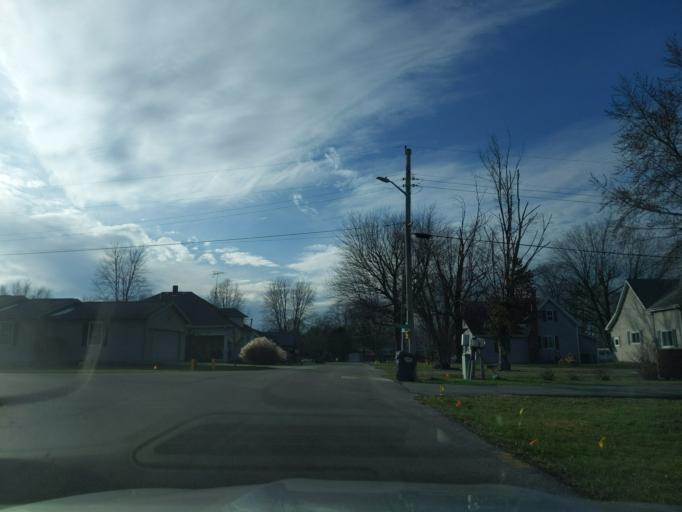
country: US
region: Indiana
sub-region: Decatur County
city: Westport
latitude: 39.1796
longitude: -85.5686
